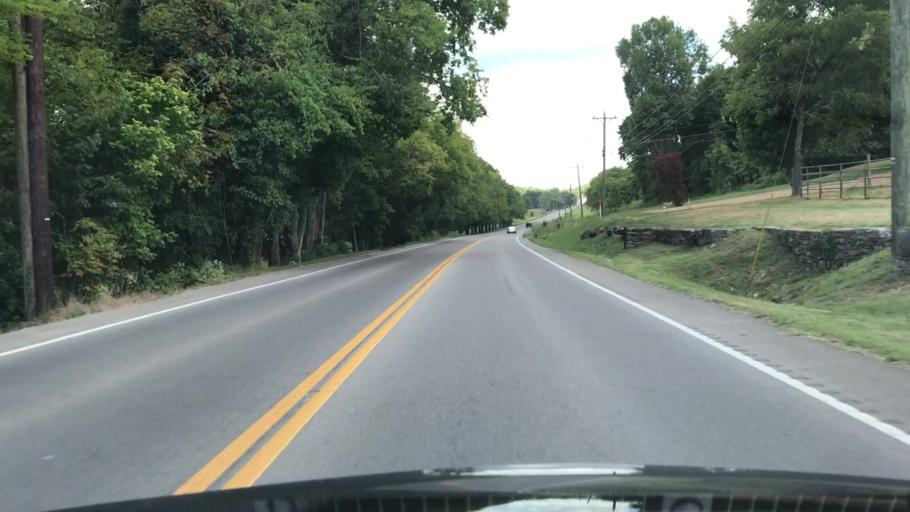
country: US
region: Tennessee
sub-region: Williamson County
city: Nolensville
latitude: 35.9023
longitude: -86.6658
